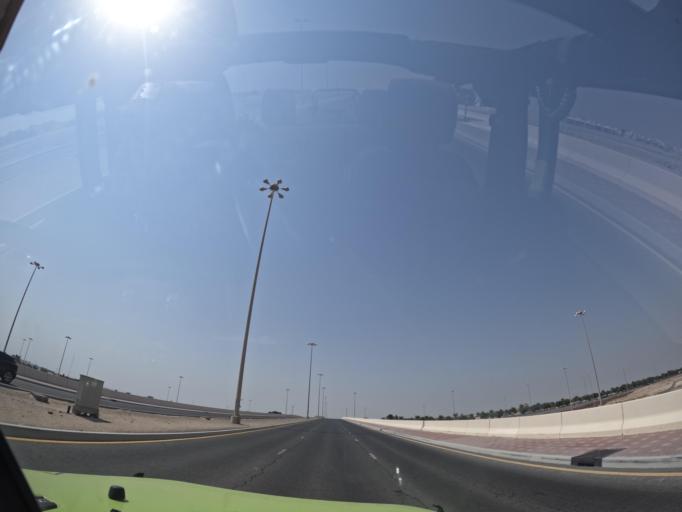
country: AE
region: Abu Dhabi
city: Abu Dhabi
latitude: 24.3388
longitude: 54.6388
